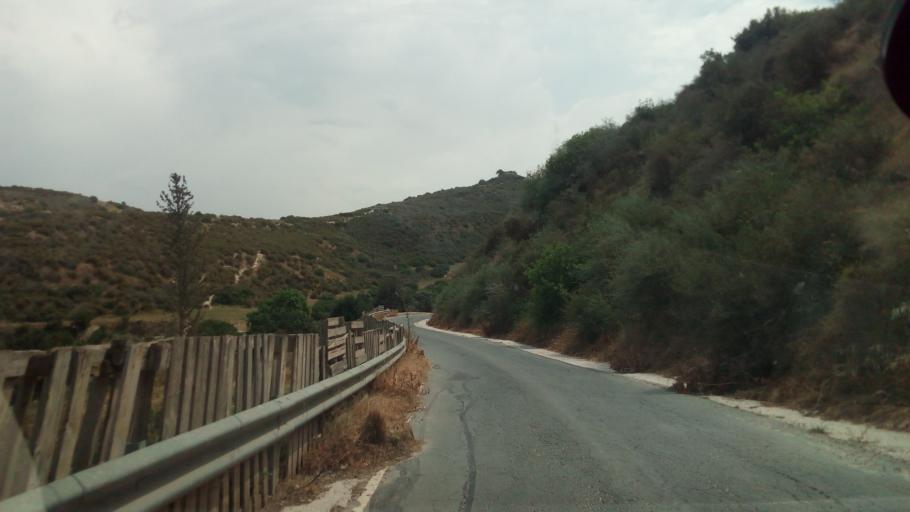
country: CY
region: Pafos
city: Polis
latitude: 35.0198
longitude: 32.3978
